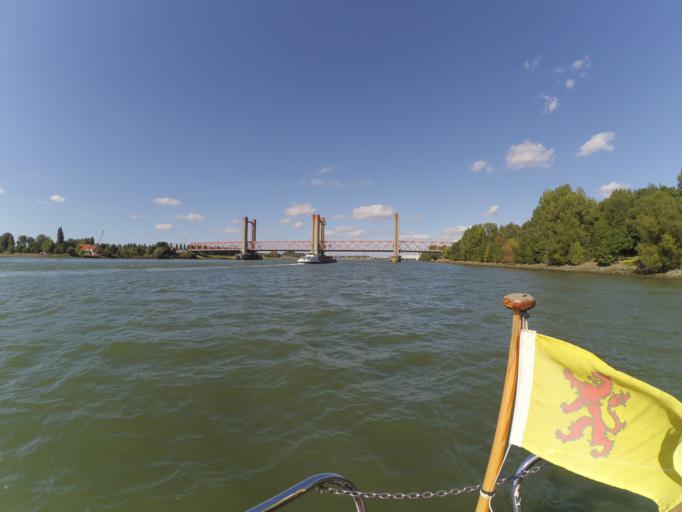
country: NL
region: South Holland
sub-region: Gemeente Spijkenisse
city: Spijkenisse
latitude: 51.8574
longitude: 4.3444
